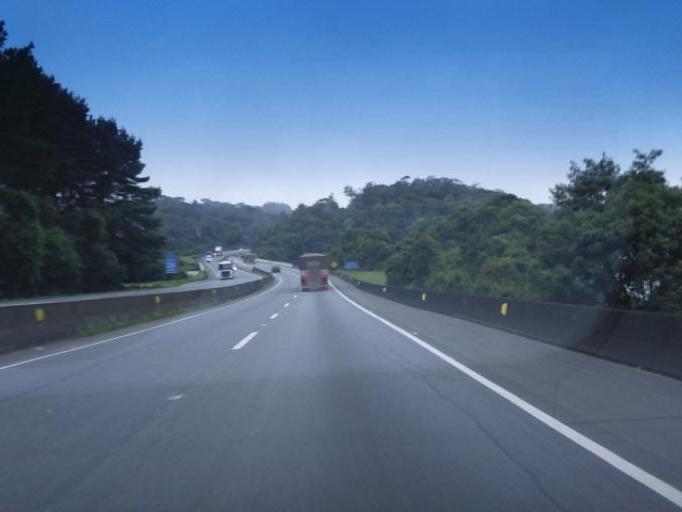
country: BR
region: Parana
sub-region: Sao Jose Dos Pinhais
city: Sao Jose dos Pinhais
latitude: -25.8452
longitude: -49.0774
